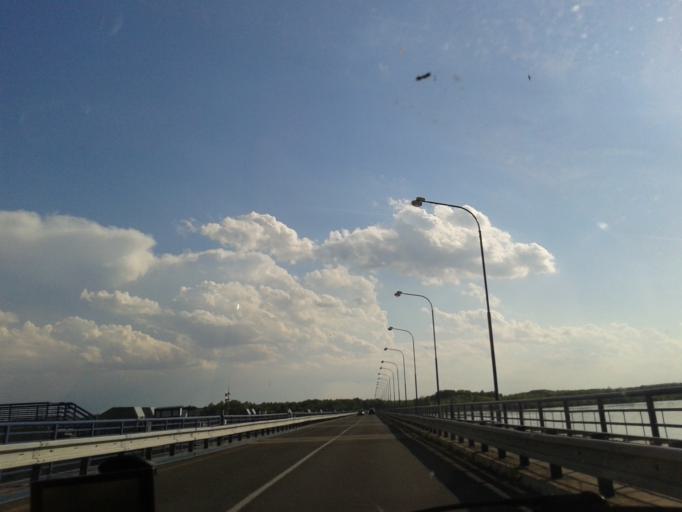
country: HU
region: Gyor-Moson-Sopron
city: Rajka
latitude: 48.0285
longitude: 17.2240
